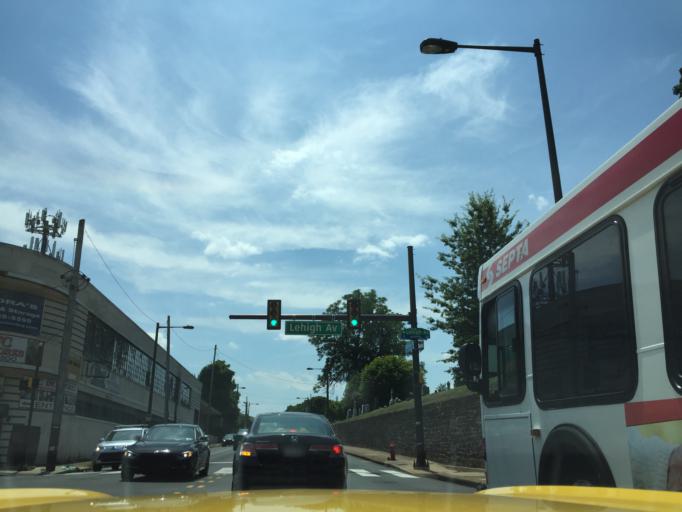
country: US
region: Pennsylvania
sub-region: Montgomery County
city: Bala-Cynwyd
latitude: 39.9983
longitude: -75.1877
